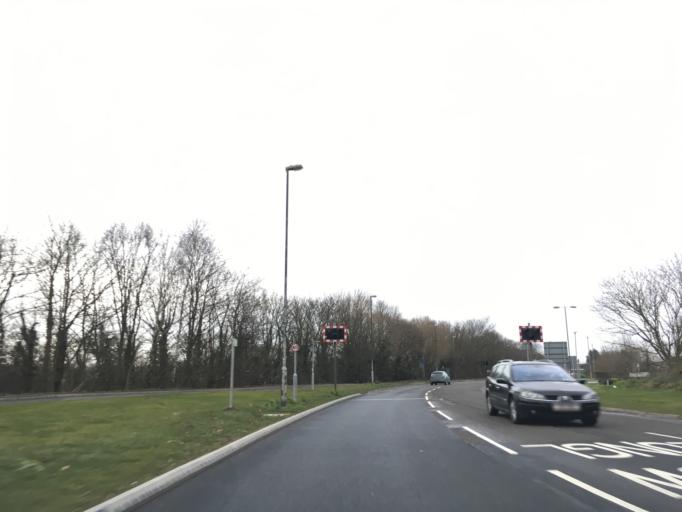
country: GB
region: England
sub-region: Gloucestershire
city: Barnwood
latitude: 51.8799
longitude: -2.2001
